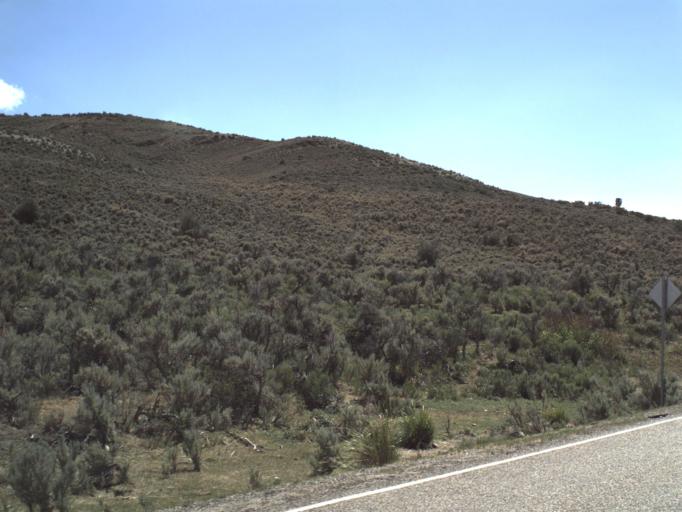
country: US
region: Utah
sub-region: Rich County
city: Randolph
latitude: 41.5040
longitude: -111.2981
